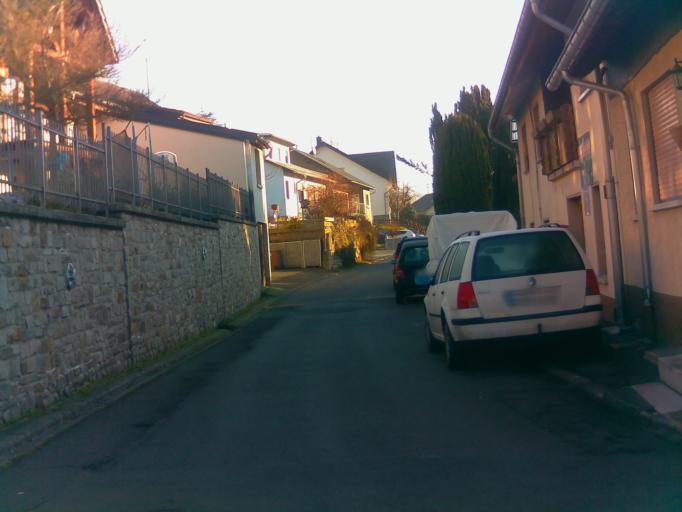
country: DE
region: Rheinland-Pfalz
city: Hochstetten-Dhaun
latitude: 49.7994
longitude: 7.5087
